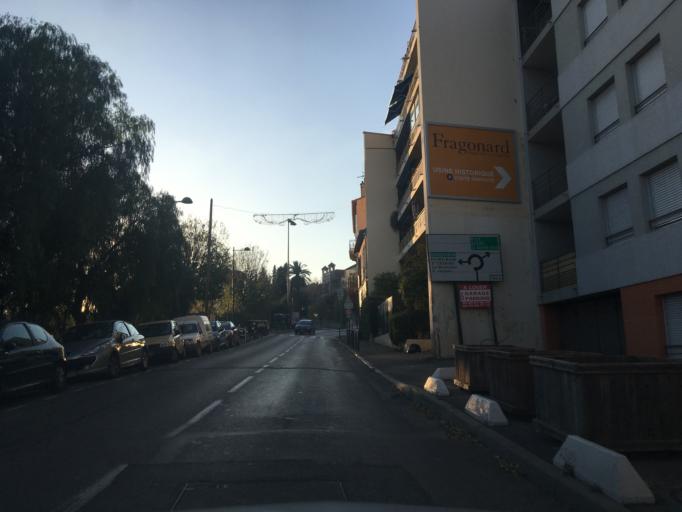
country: FR
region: Provence-Alpes-Cote d'Azur
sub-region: Departement des Alpes-Maritimes
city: Grasse
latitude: 43.6500
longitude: 6.9191
